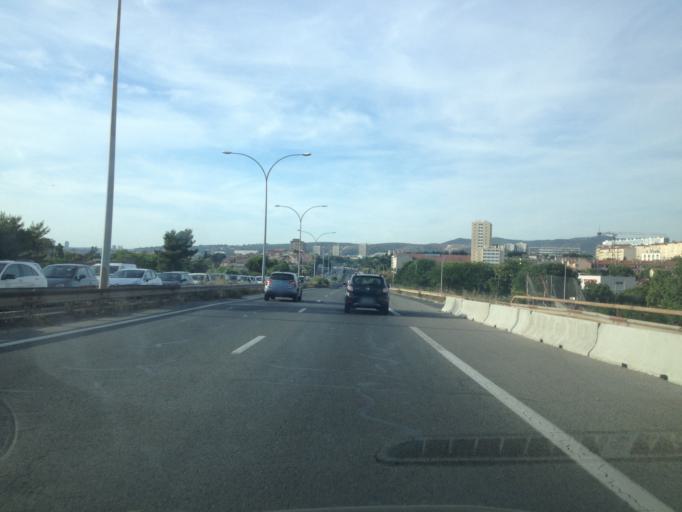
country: FR
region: Provence-Alpes-Cote d'Azur
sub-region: Departement des Bouches-du-Rhone
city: Marseille 03
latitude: 43.3171
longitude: 5.3772
